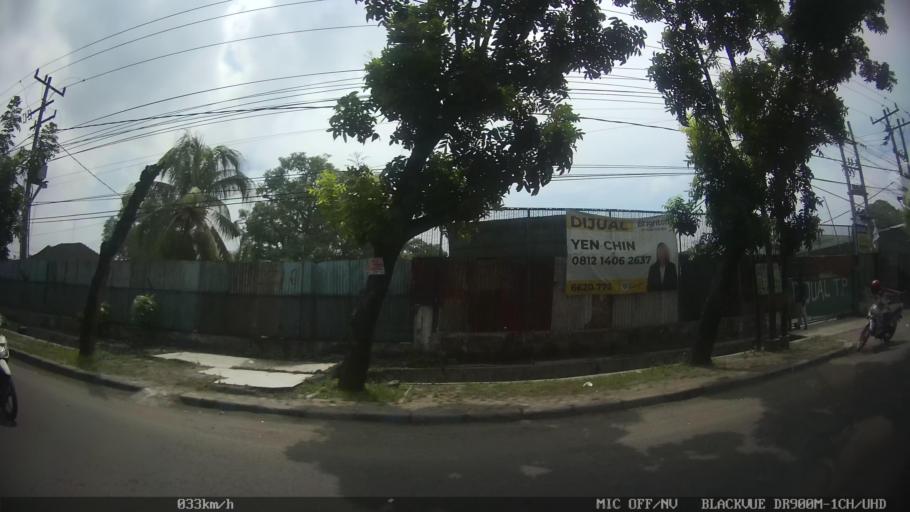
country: ID
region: North Sumatra
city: Medan
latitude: 3.6448
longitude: 98.6626
